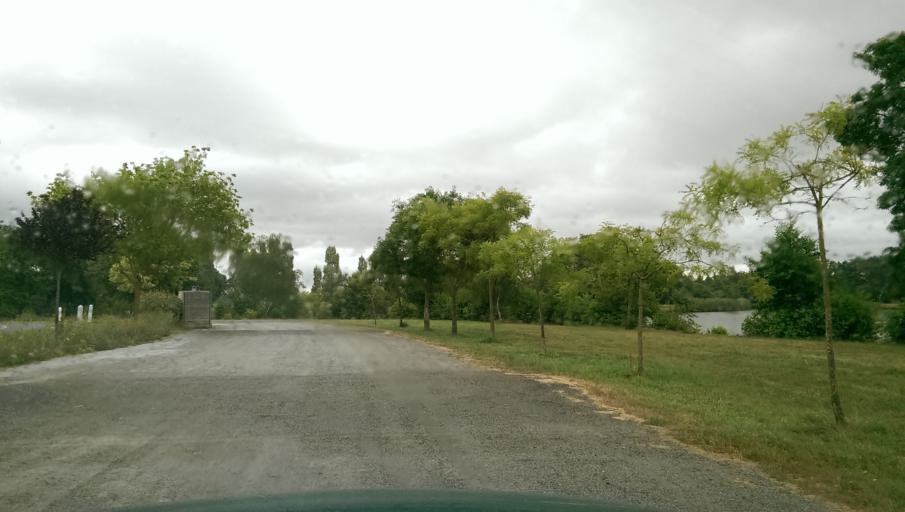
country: FR
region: Pays de la Loire
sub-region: Departement de la Loire-Atlantique
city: La Planche
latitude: 47.0168
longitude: -1.4159
